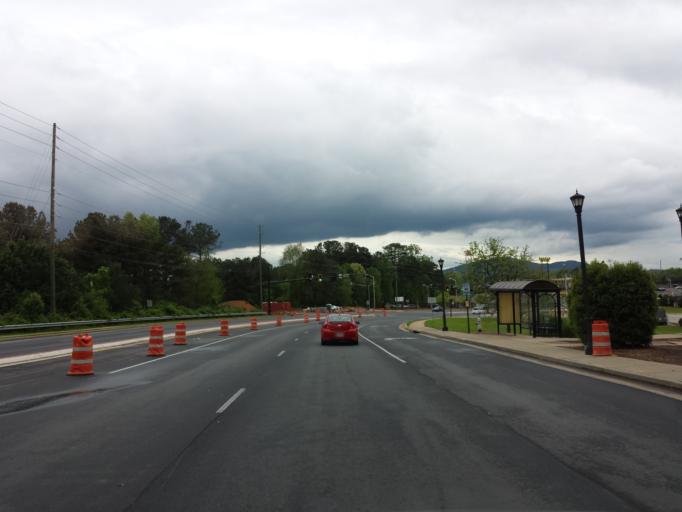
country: US
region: Georgia
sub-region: Cobb County
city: Kennesaw
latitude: 34.0377
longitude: -84.5795
